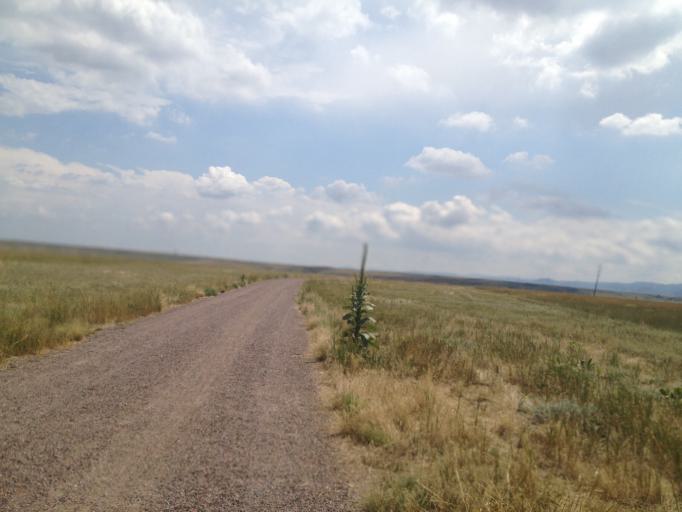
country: US
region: Colorado
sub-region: Boulder County
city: Superior
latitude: 39.9390
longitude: -105.1698
